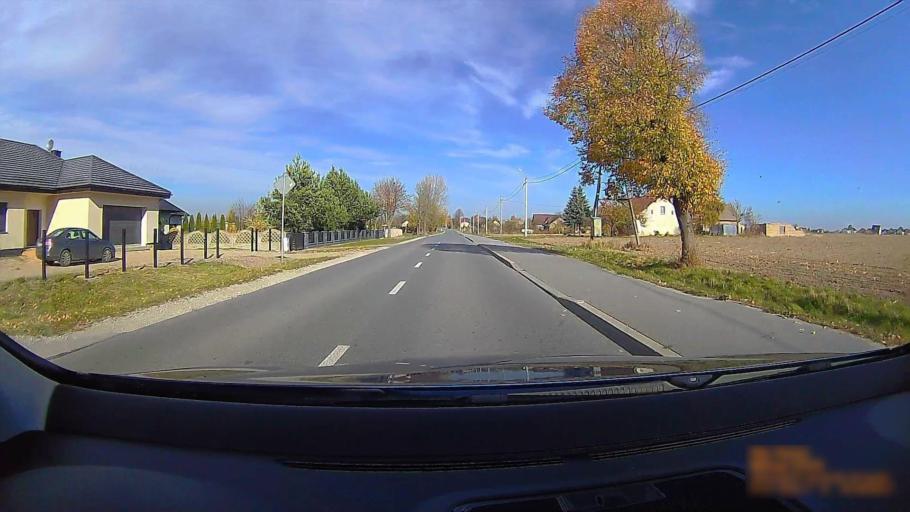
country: PL
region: Greater Poland Voivodeship
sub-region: Powiat kepinski
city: Kepno
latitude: 51.3285
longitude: 18.0165
